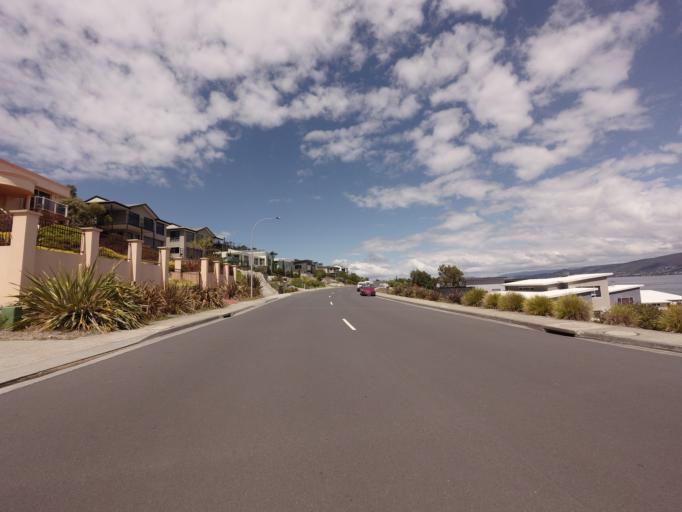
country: AU
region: Tasmania
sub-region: Clarence
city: Howrah
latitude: -42.9052
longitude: 147.4217
